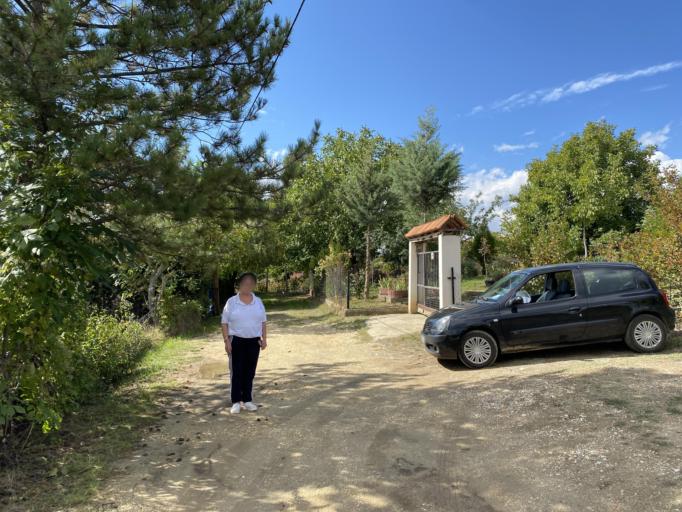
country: MK
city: Radishani
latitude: 42.0831
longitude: 21.4504
